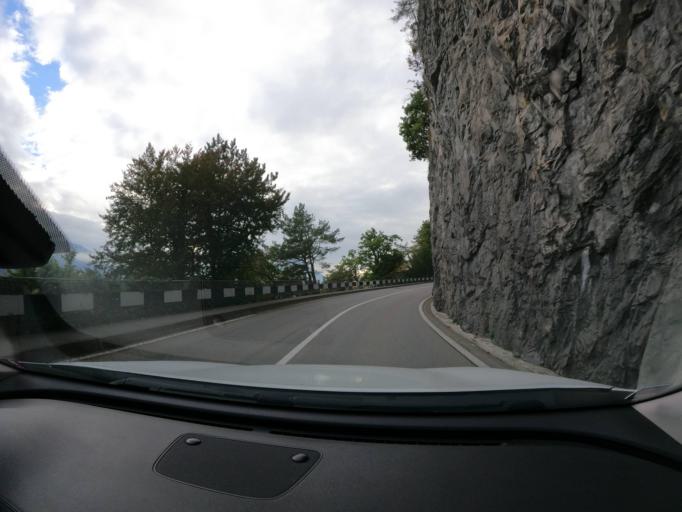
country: CH
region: Bern
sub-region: Interlaken-Oberhasli District
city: Beatenberg
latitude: 46.6839
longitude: 7.8033
